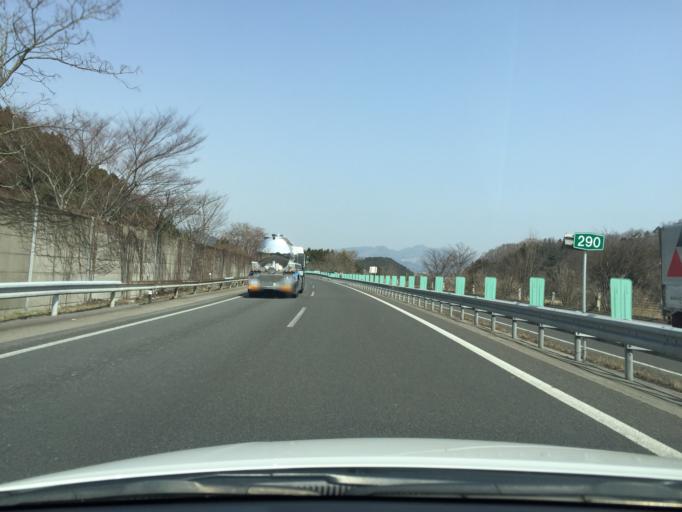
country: JP
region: Miyagi
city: Shiroishi
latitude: 37.9623
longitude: 140.6200
